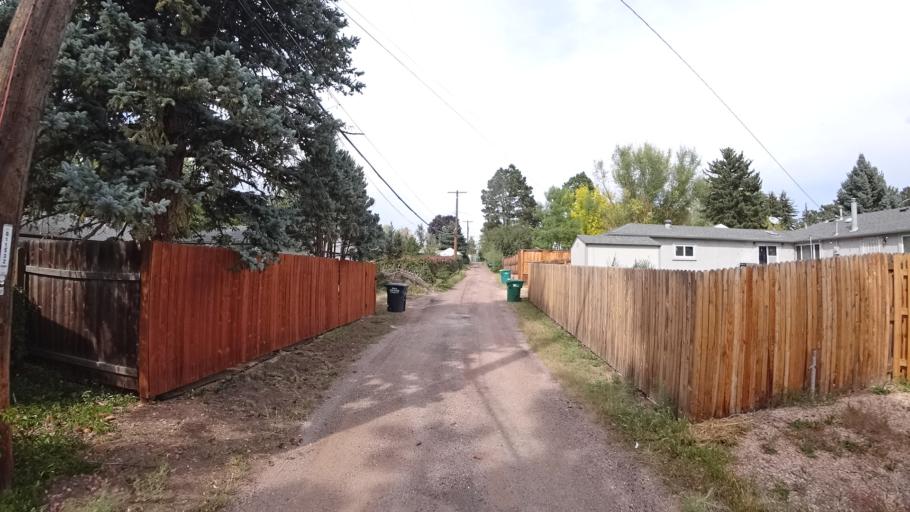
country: US
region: Colorado
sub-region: El Paso County
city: Colorado Springs
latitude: 38.8630
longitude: -104.7912
